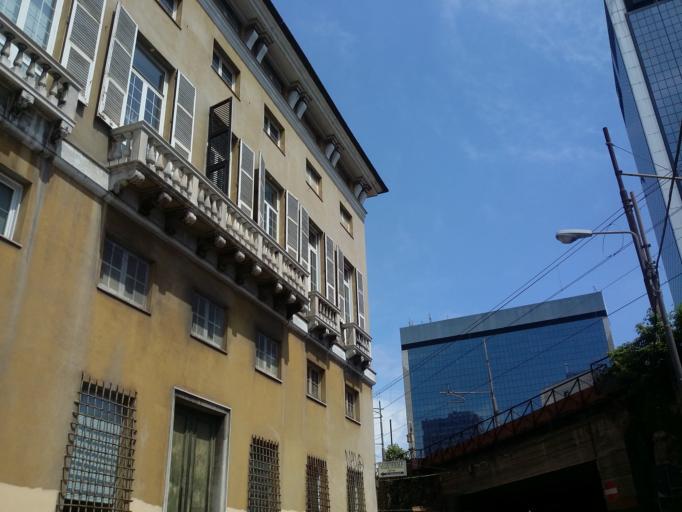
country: IT
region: Liguria
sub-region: Provincia di Genova
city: San Teodoro
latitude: 44.4092
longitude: 8.8994
